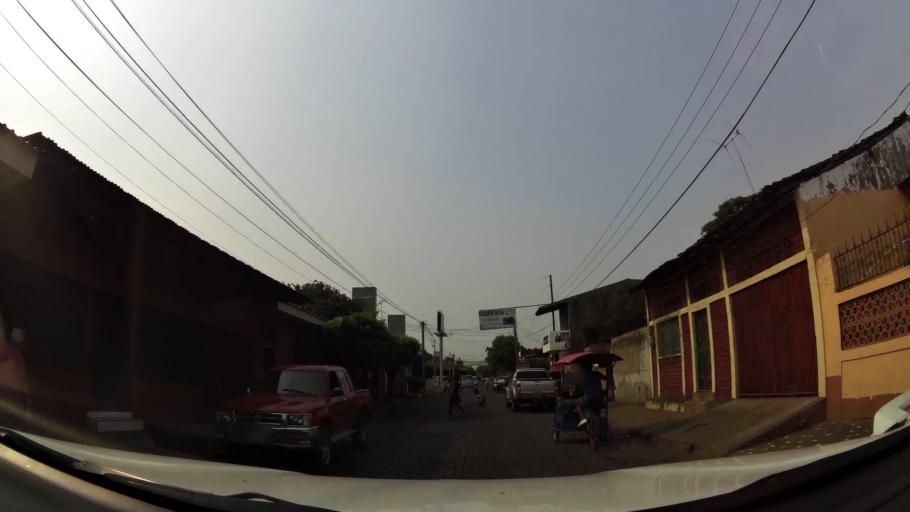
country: NI
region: Chinandega
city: Chinandega
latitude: 12.6293
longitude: -87.1231
